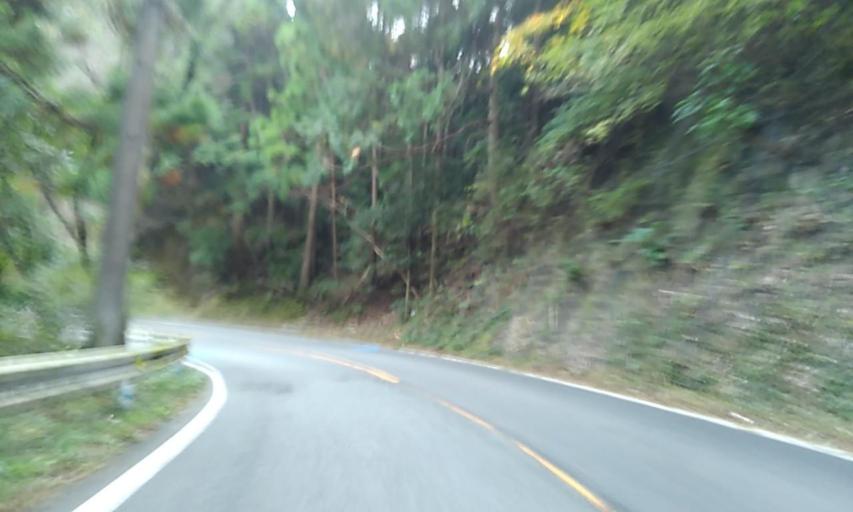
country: JP
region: Mie
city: Ise
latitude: 34.2890
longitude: 136.5348
